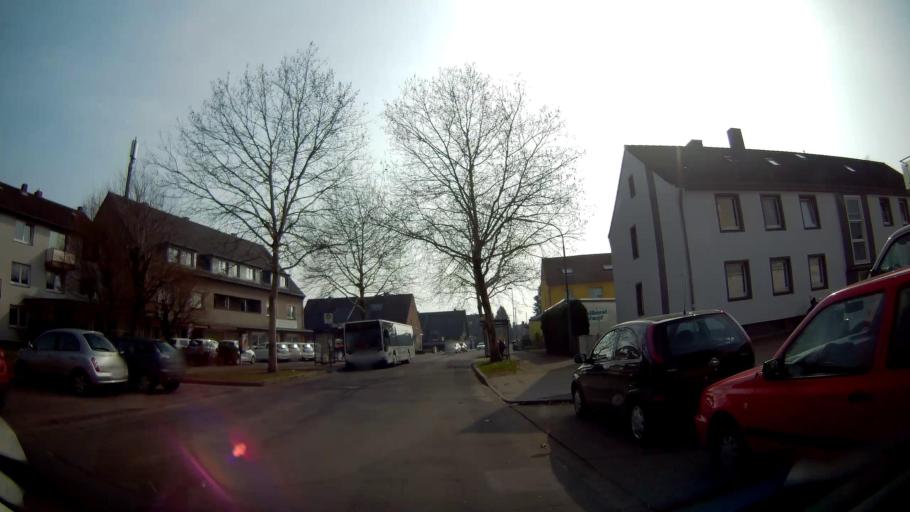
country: DE
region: North Rhine-Westphalia
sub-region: Regierungsbezirk Dusseldorf
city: Moers
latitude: 51.4857
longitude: 6.6376
